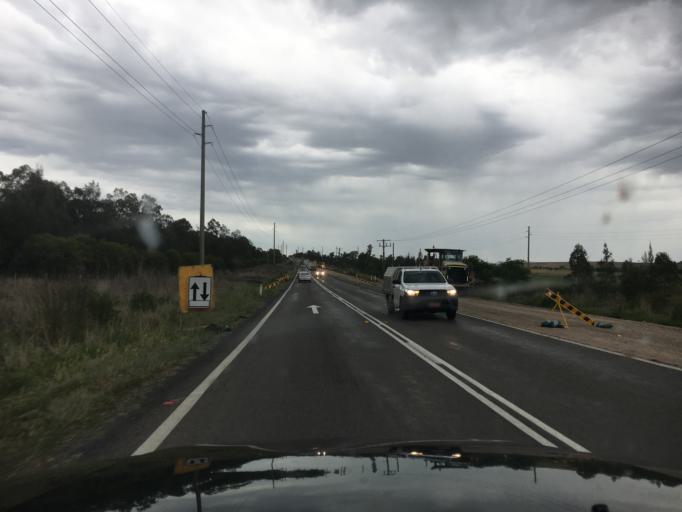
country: AU
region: New South Wales
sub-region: Muswellbrook
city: Muswellbrook
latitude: -32.1947
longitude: 150.8931
